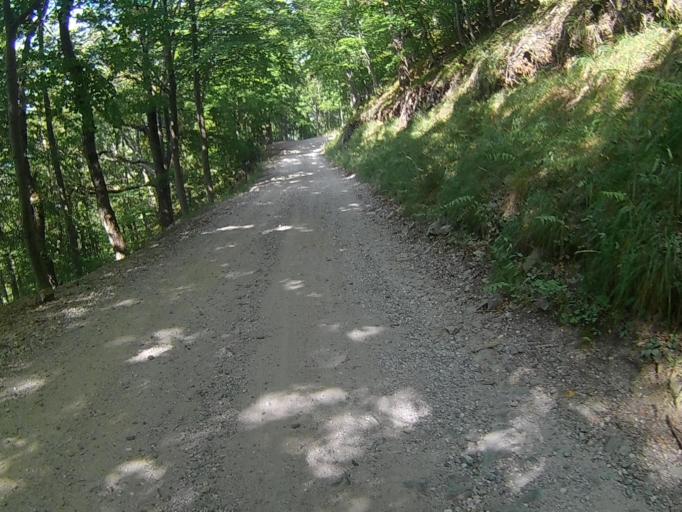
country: SI
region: Ruse
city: Bistrica ob Dravi
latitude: 46.5192
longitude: 15.5540
